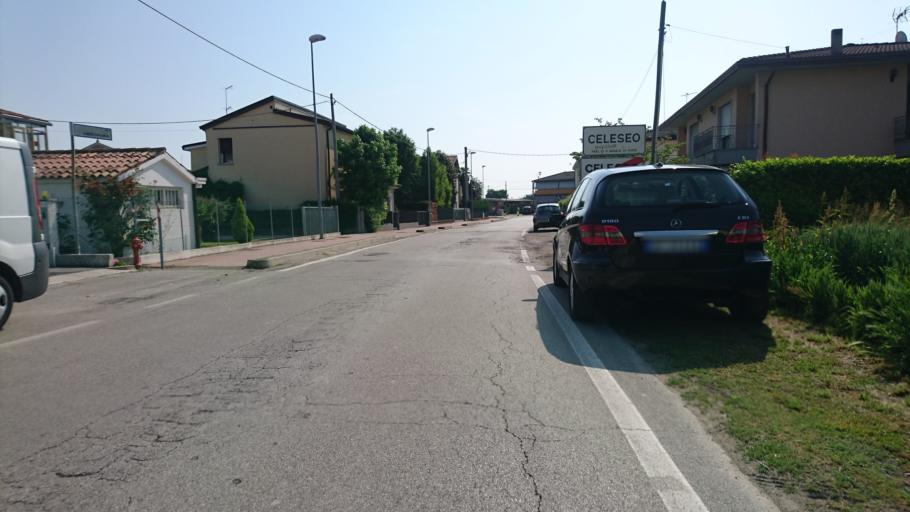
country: IT
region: Veneto
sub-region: Provincia di Venezia
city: Vigonovo
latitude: 45.3687
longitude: 12.0116
